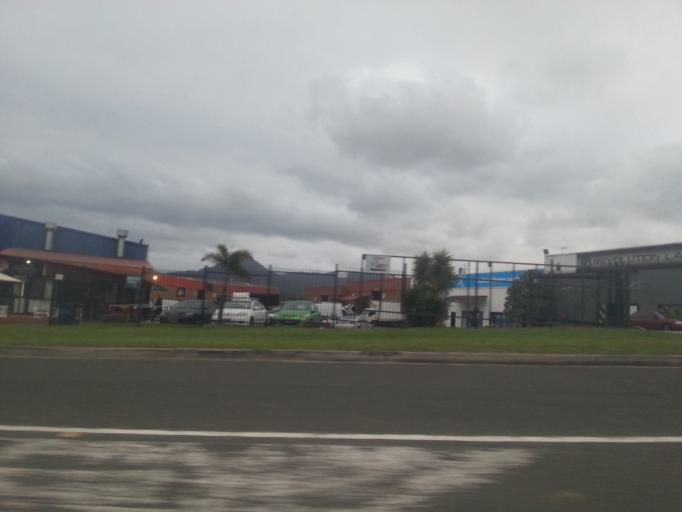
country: AU
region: New South Wales
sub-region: Wollongong
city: Mount Saint Thomas
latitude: -34.4440
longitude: 150.8725
